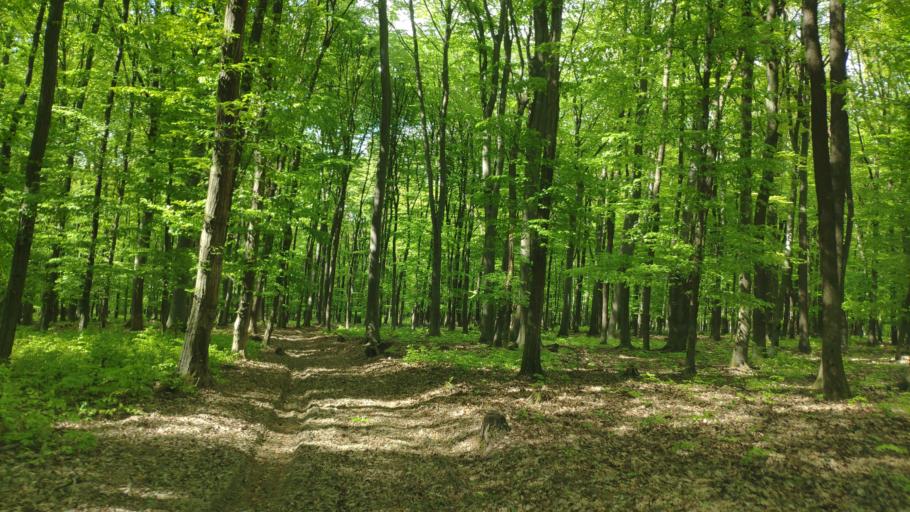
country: SK
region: Kosicky
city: Kosice
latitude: 48.6702
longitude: 21.4471
